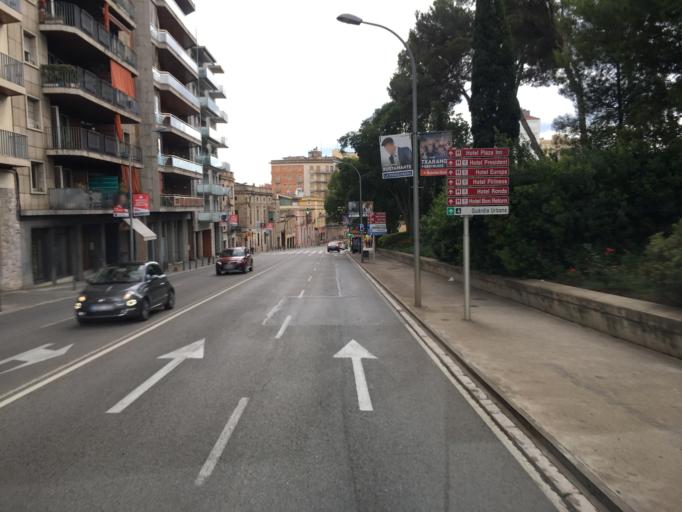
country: ES
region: Catalonia
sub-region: Provincia de Girona
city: Figueres
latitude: 42.2675
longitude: 2.9578
